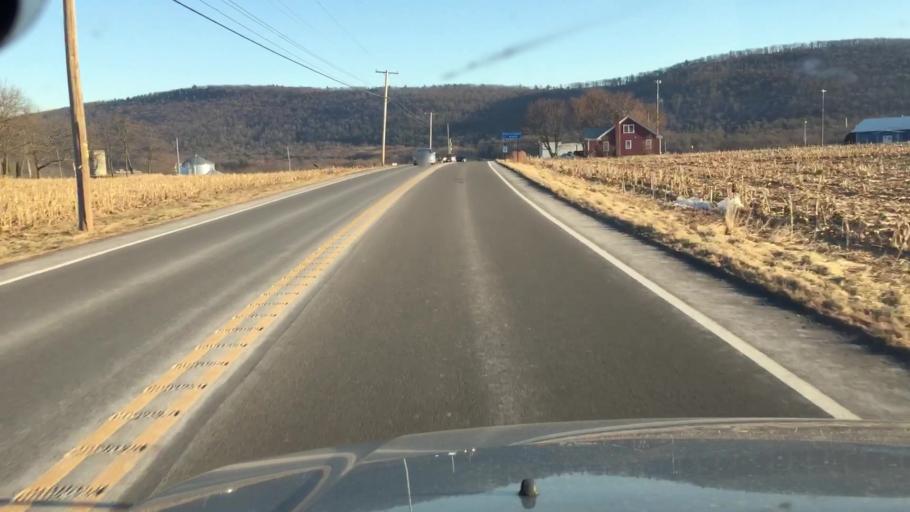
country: US
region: Pennsylvania
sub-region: Luzerne County
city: Nescopeck
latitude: 41.0427
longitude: -76.1424
